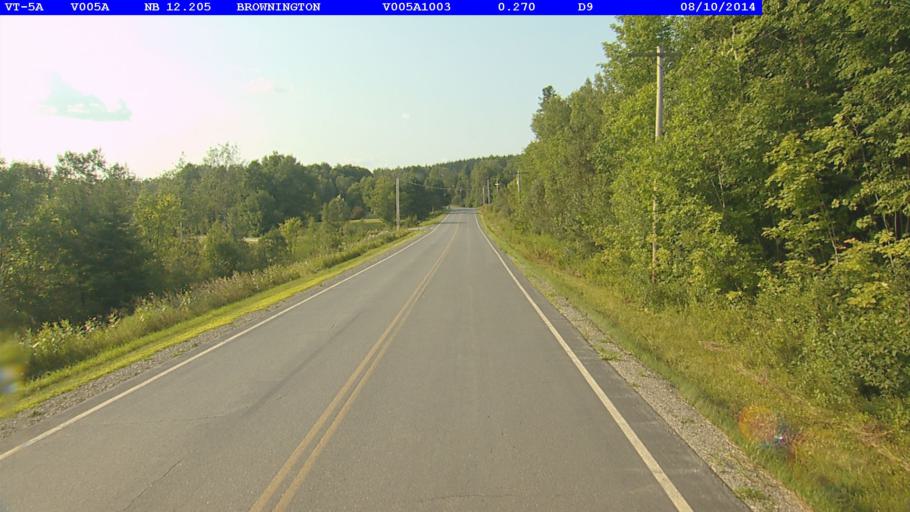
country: US
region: Vermont
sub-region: Orleans County
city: Newport
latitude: 44.7910
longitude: -72.0779
